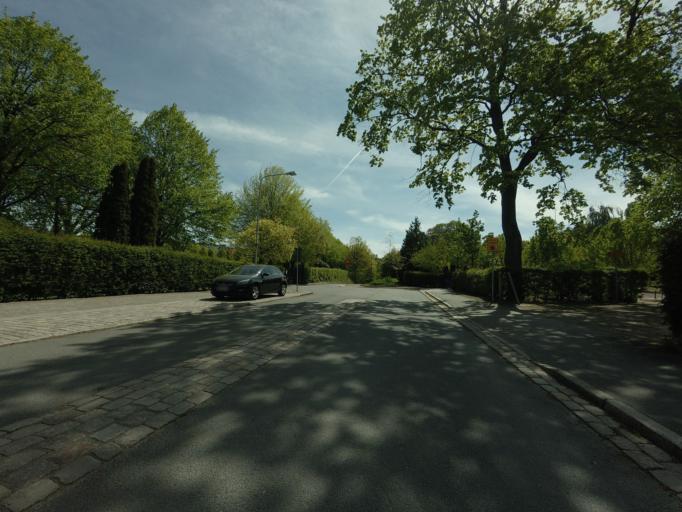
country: SE
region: Skane
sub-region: Helsingborg
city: Helsingborg
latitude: 56.0433
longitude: 12.7042
